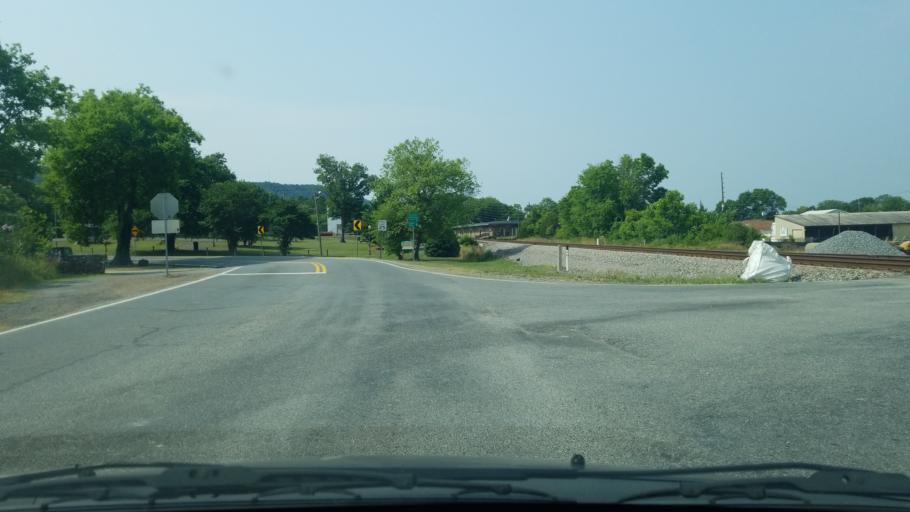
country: US
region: Georgia
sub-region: Catoosa County
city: Ringgold
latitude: 34.9175
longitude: -85.1067
